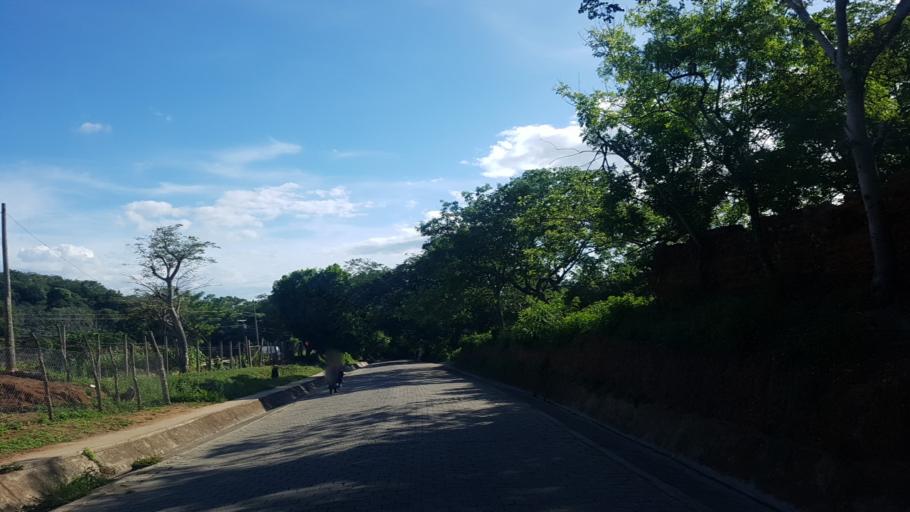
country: NI
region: Nueva Segovia
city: Mozonte
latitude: 13.6562
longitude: -86.4402
